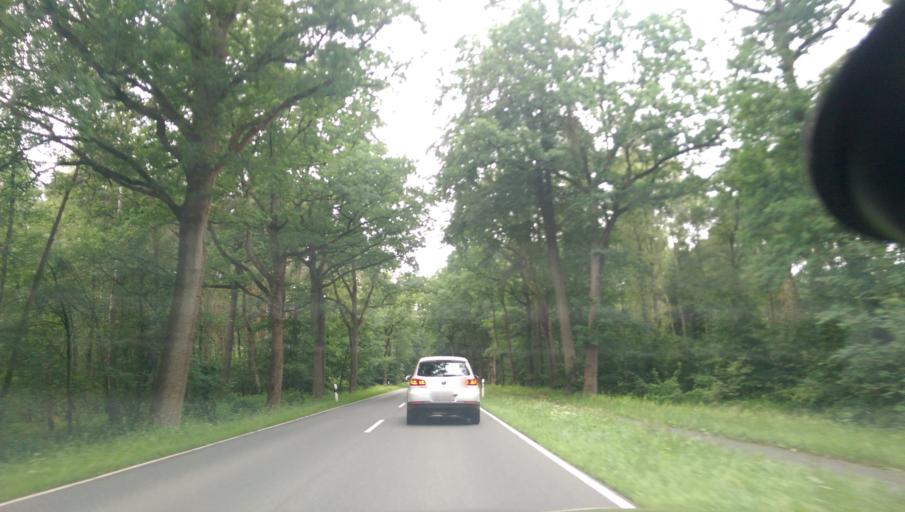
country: DE
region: Lower Saxony
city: Rotenburg
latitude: 53.0802
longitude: 9.4272
